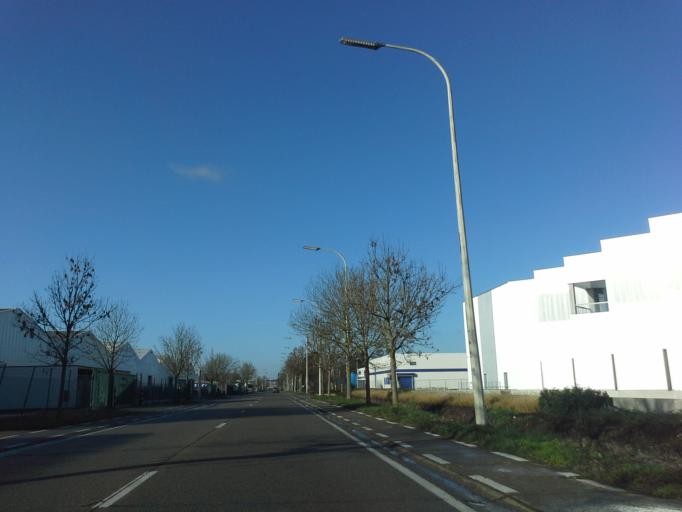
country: BE
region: Flanders
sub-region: Provincie Antwerpen
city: Herentals
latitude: 51.1627
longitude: 4.8039
